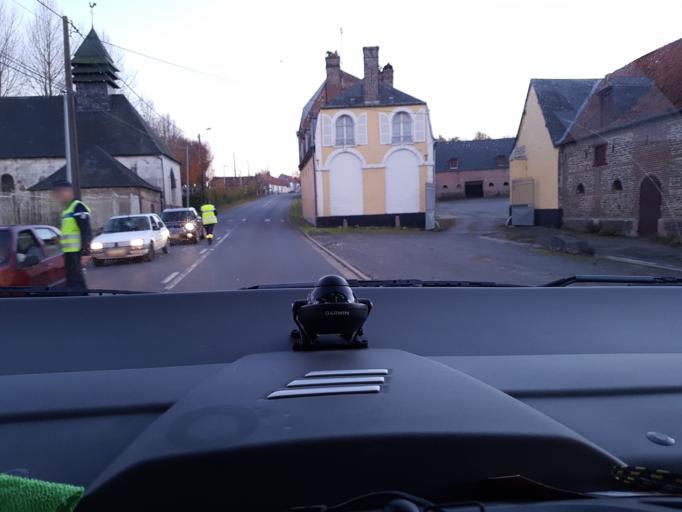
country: FR
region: Picardie
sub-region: Departement de la Somme
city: Rue
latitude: 50.2704
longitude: 1.7434
